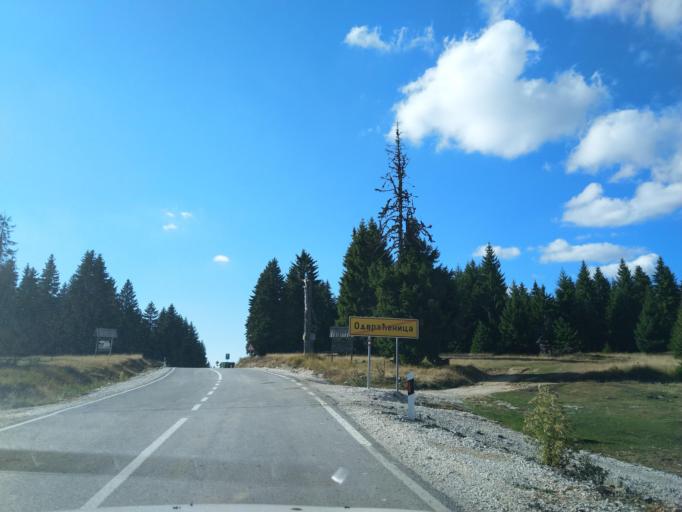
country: RS
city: Sokolovica
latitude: 43.2809
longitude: 20.3343
